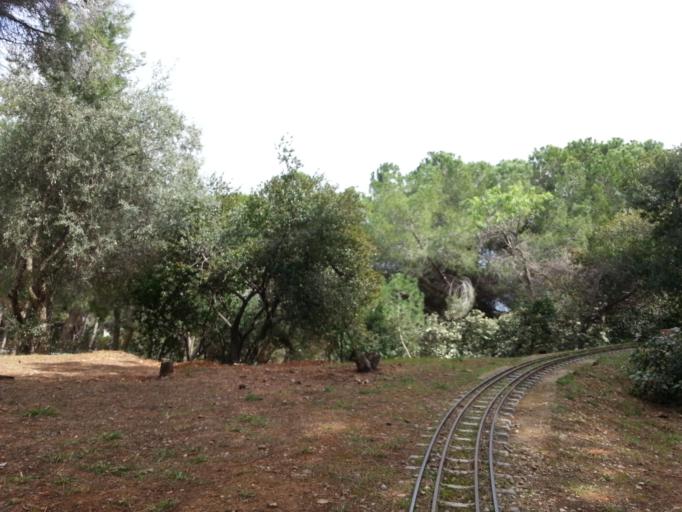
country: ES
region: Catalonia
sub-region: Provincia de Barcelona
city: les Corts
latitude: 41.4010
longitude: 2.1085
